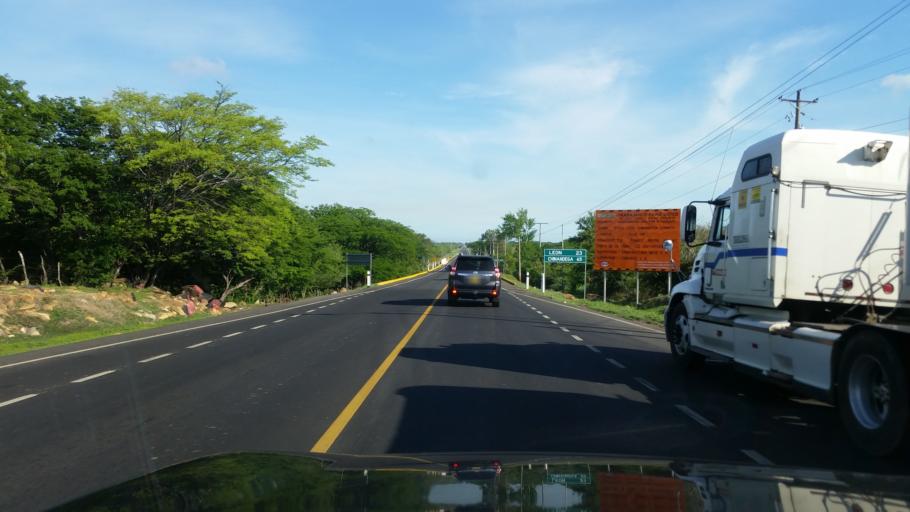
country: NI
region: Leon
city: La Paz Centro
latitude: 12.2682
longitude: -86.7369
